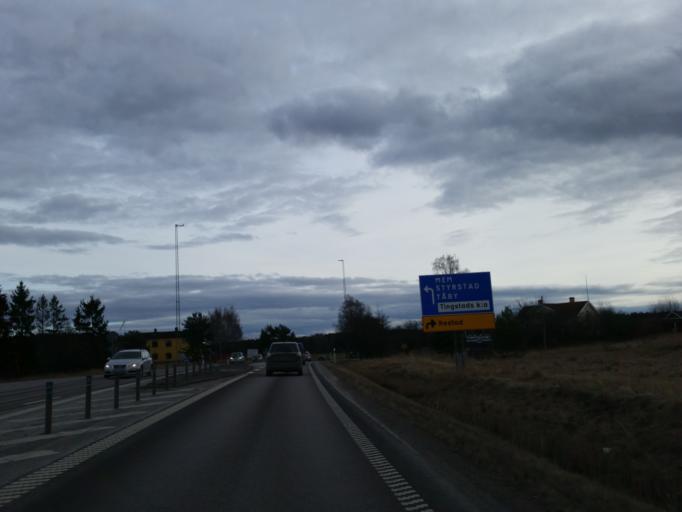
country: SE
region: OEstergoetland
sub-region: Soderkopings Kommun
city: Soederkoeping
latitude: 58.5312
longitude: 16.2858
